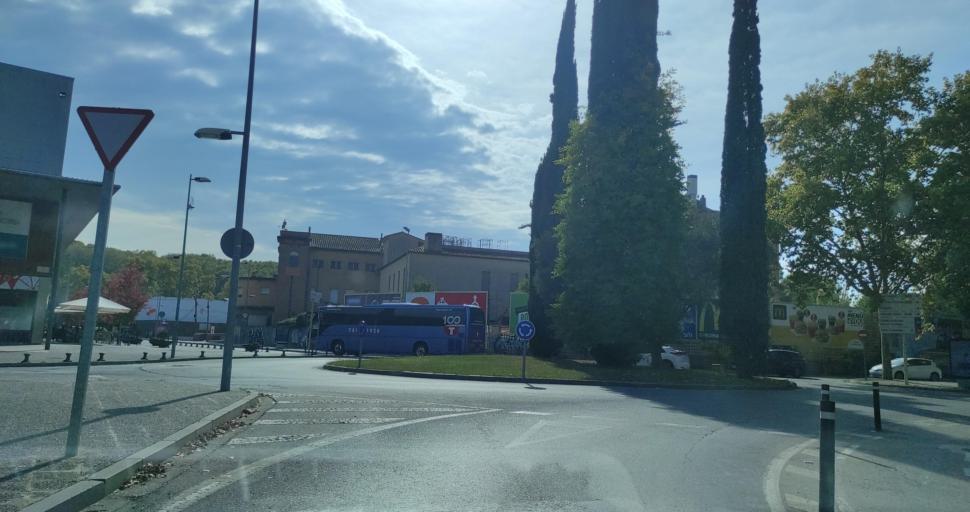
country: ES
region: Catalonia
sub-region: Provincia de Girona
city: Girona
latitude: 41.9925
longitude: 2.8184
